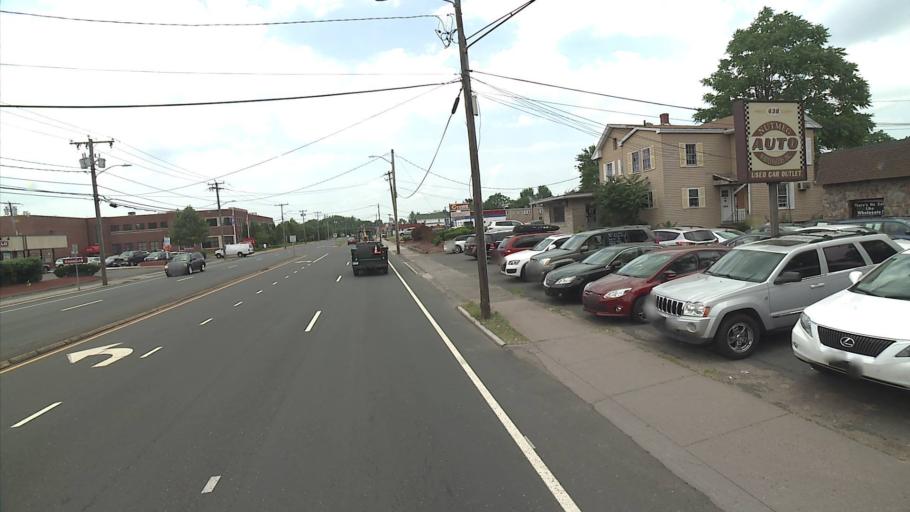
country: US
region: Connecticut
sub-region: Hartford County
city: Wethersfield
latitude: 41.7528
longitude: -72.6405
